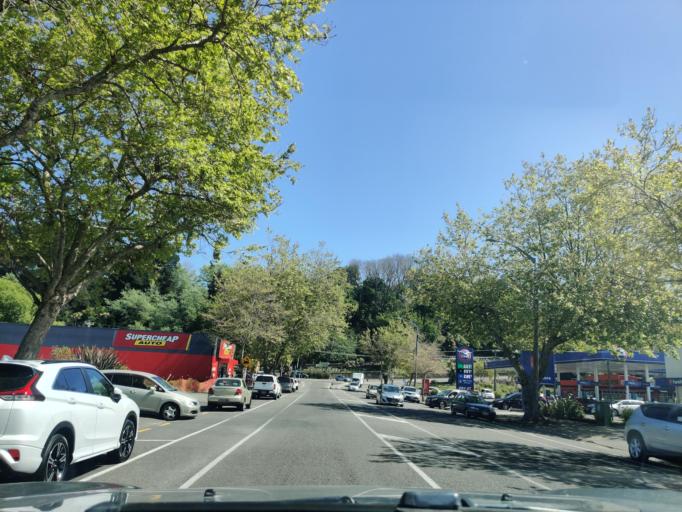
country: NZ
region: Manawatu-Wanganui
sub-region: Wanganui District
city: Wanganui
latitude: -39.9249
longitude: 175.0385
